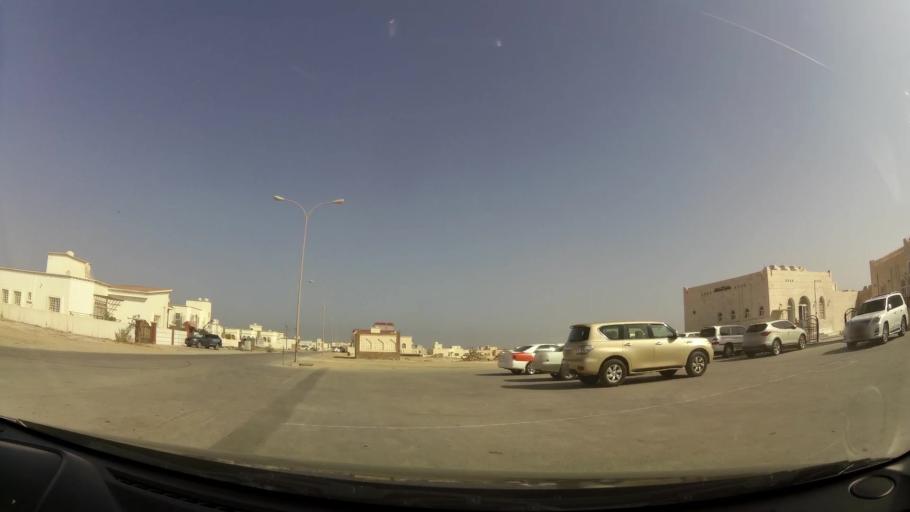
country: OM
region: Zufar
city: Salalah
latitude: 17.0082
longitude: 54.0036
